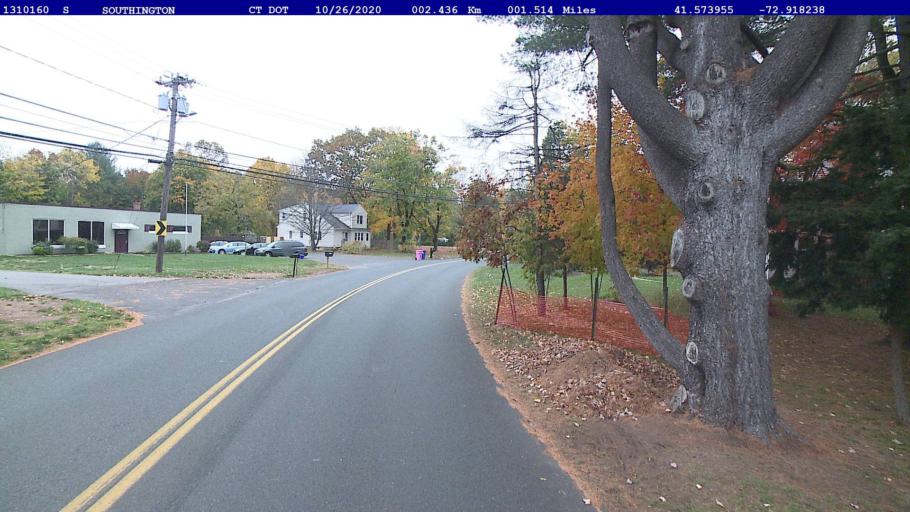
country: US
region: Connecticut
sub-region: New Haven County
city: Cheshire Village
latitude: 41.5740
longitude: -72.9182
